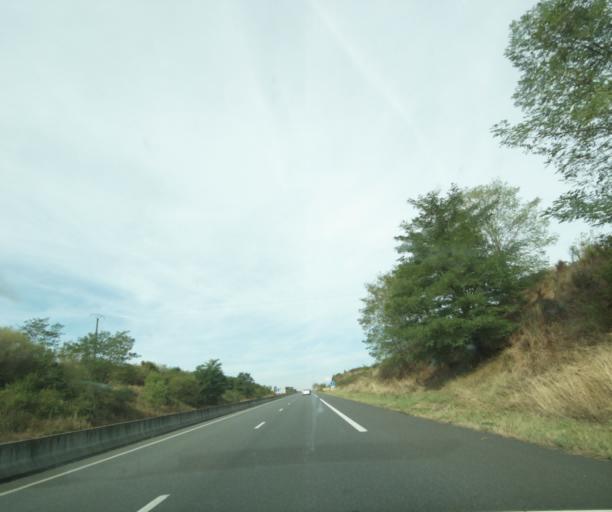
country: FR
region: Auvergne
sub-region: Departement de l'Allier
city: Lapalisse
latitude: 46.2375
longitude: 3.6261
